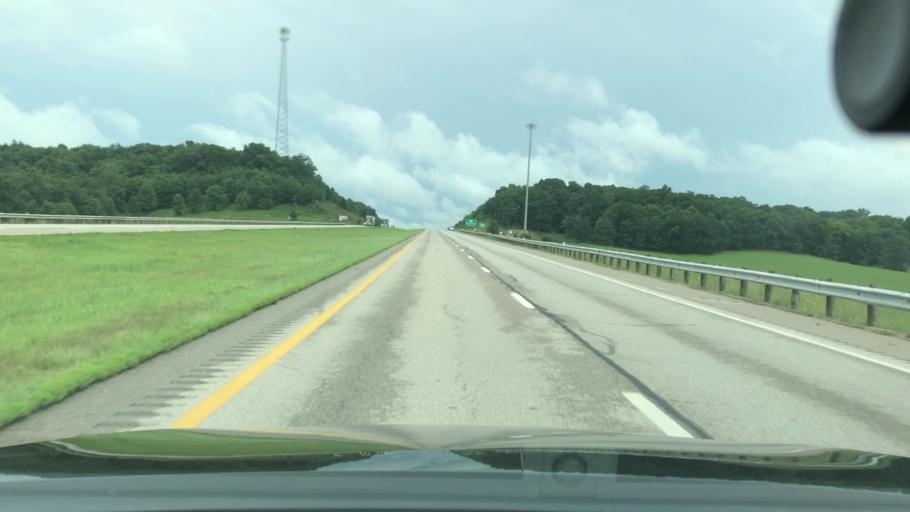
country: US
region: Ohio
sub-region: Gallia County
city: Gallipolis
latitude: 38.8799
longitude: -82.3172
